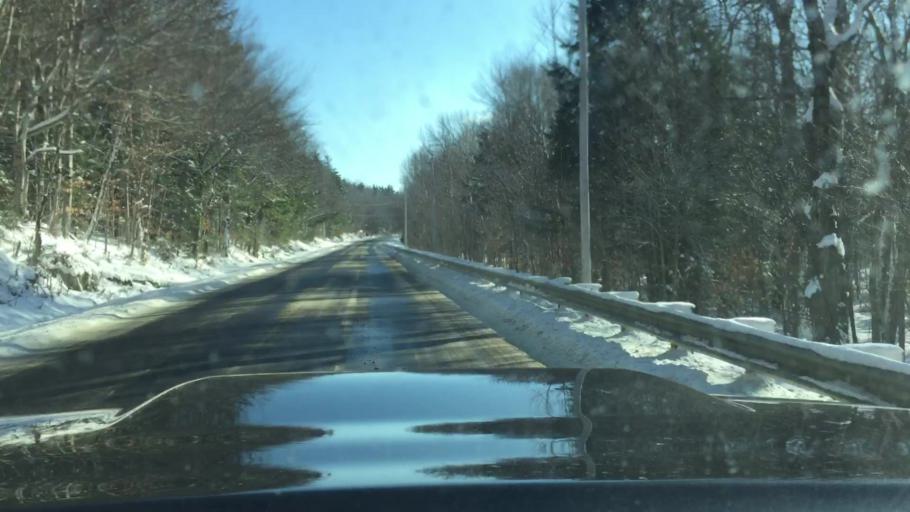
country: US
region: Massachusetts
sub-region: Berkshire County
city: Hinsdale
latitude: 42.4569
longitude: -72.9840
